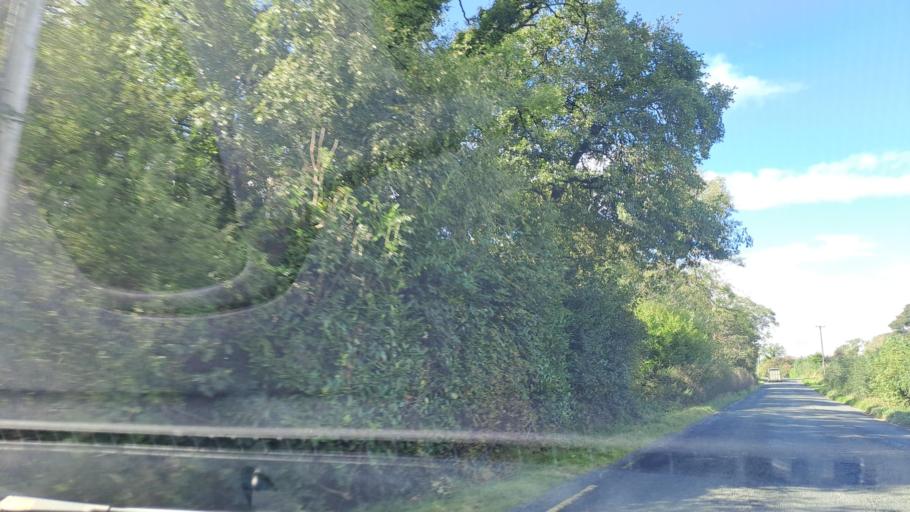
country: IE
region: Ulster
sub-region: An Cabhan
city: Kingscourt
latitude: 53.9644
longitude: -6.8583
